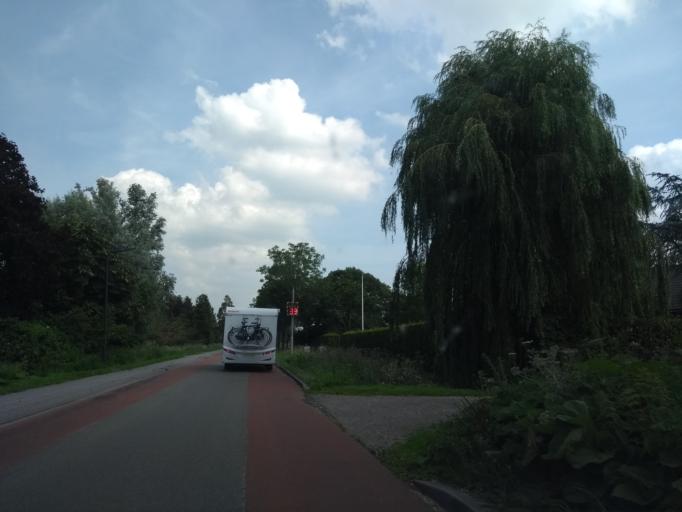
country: NL
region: Friesland
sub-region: Sudwest Fryslan
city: Oppenhuizen
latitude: 53.0320
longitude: 5.6974
